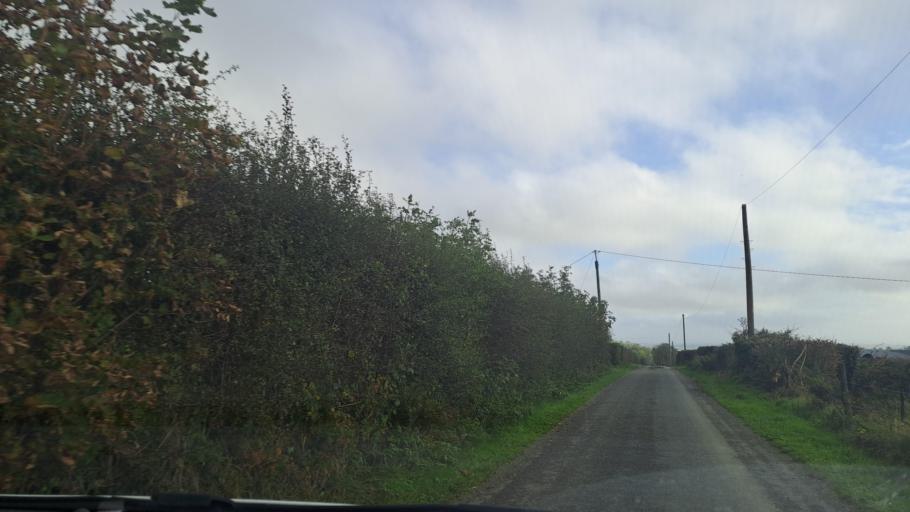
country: IE
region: Ulster
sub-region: County Monaghan
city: Carrickmacross
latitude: 54.0245
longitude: -6.7704
